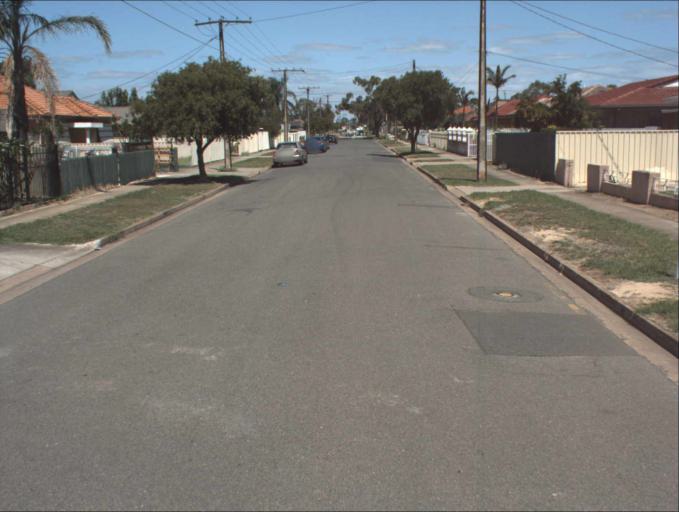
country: AU
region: South Australia
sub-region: Charles Sturt
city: Woodville North
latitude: -34.8525
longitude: 138.5491
